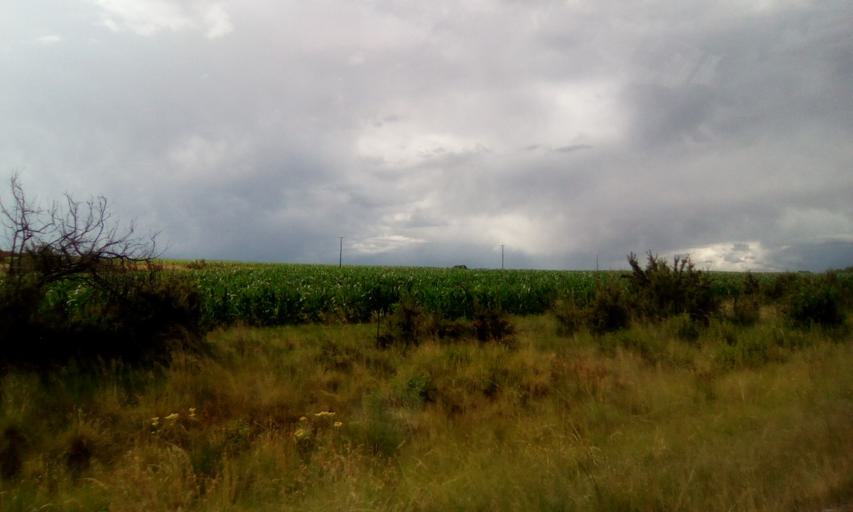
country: ZA
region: Orange Free State
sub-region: Thabo Mofutsanyana District Municipality
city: Ladybrand
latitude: -29.2429
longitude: 27.4482
